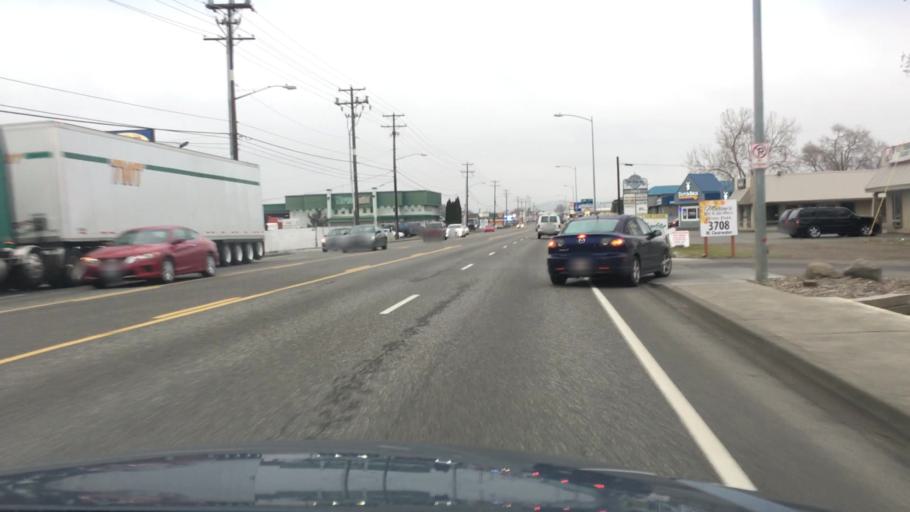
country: US
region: Washington
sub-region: Benton County
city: Kennewick
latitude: 46.2124
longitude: -119.1715
